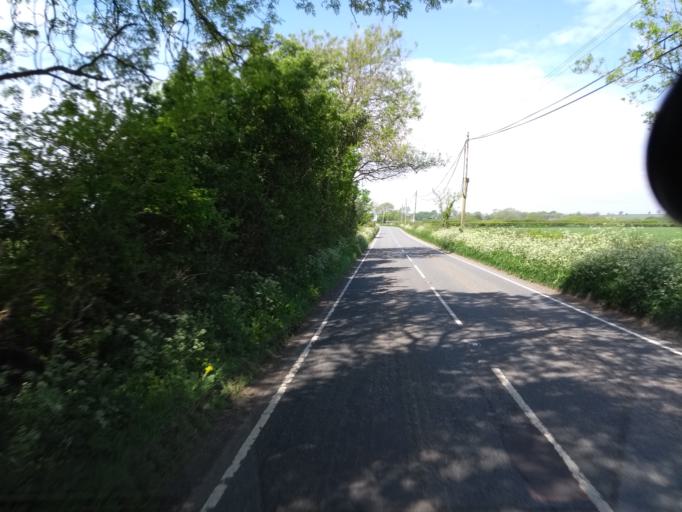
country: GB
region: England
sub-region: Somerset
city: Chard
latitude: 50.8806
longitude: -2.9957
